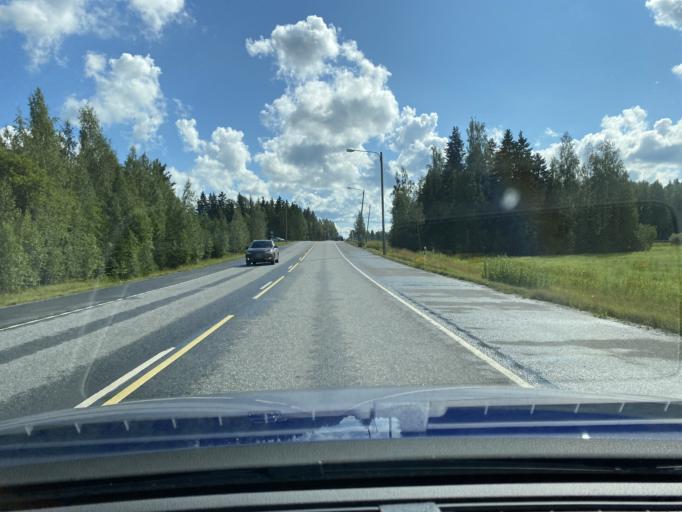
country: FI
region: Pirkanmaa
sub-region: Tampere
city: Lempaeaelae
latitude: 61.3281
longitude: 23.7752
